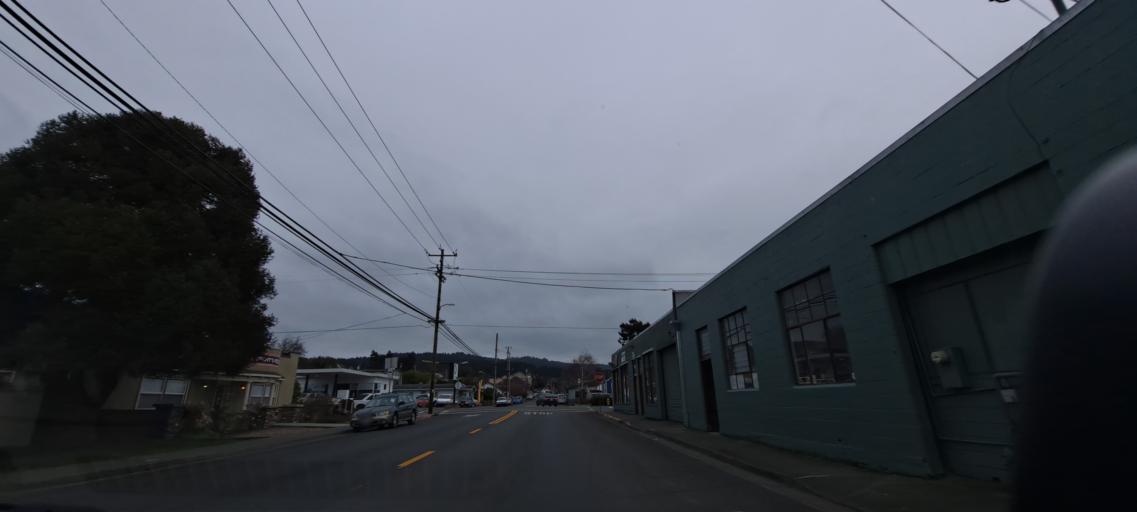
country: US
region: California
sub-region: Humboldt County
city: Arcata
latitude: 40.8714
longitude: -124.0901
